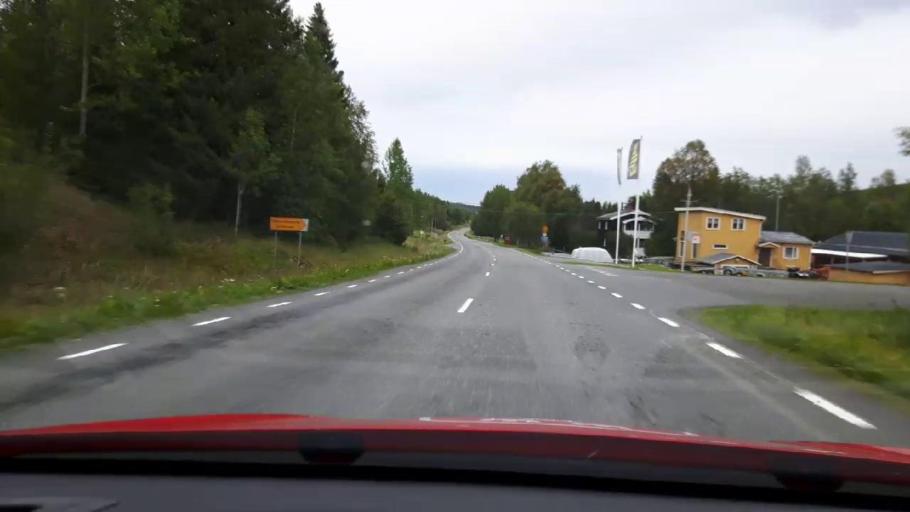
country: SE
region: Jaemtland
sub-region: Are Kommun
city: Jarpen
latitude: 63.3920
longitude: 13.3889
